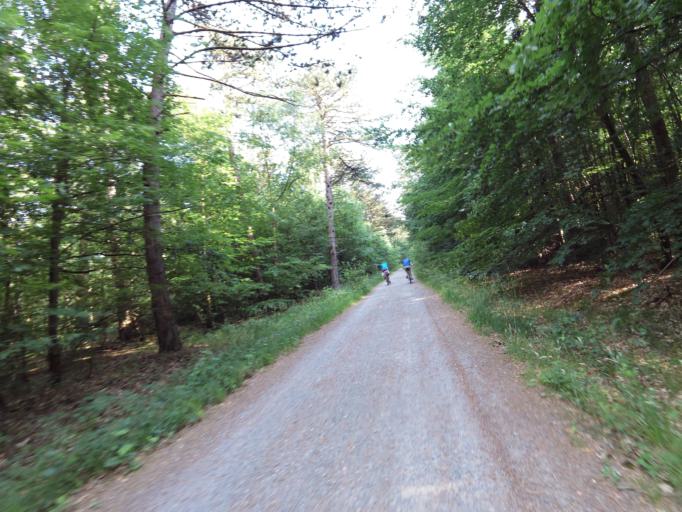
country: DE
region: Lower Saxony
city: Nordholz
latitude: 53.8561
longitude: 8.6015
